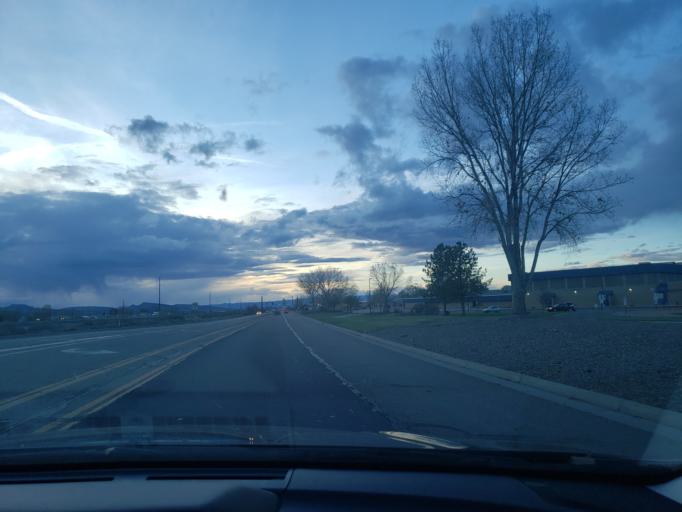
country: US
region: Colorado
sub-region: Mesa County
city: Fruita
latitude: 39.1467
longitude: -108.7161
